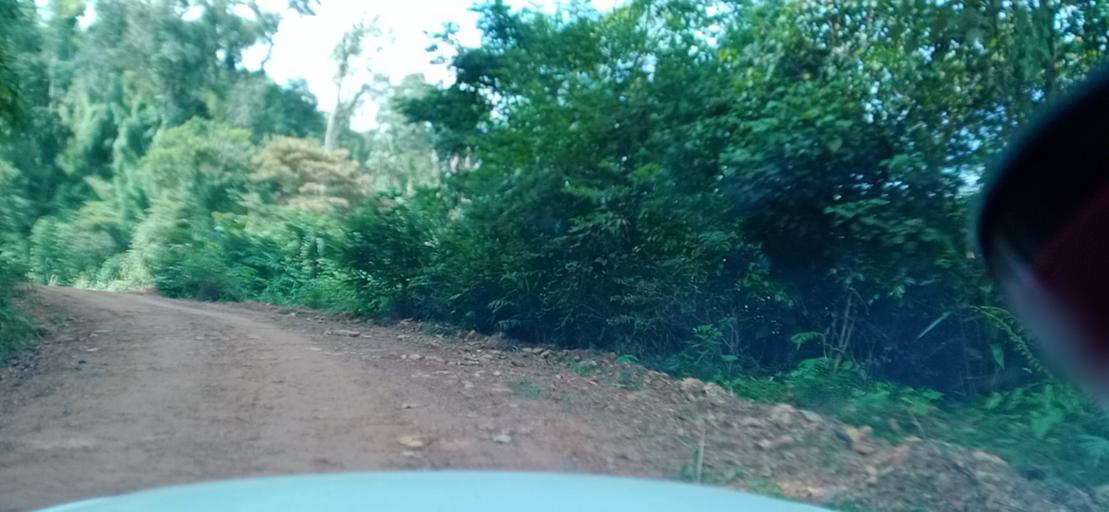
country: TH
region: Changwat Bueng Kan
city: Pak Khat
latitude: 18.6375
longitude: 103.2589
